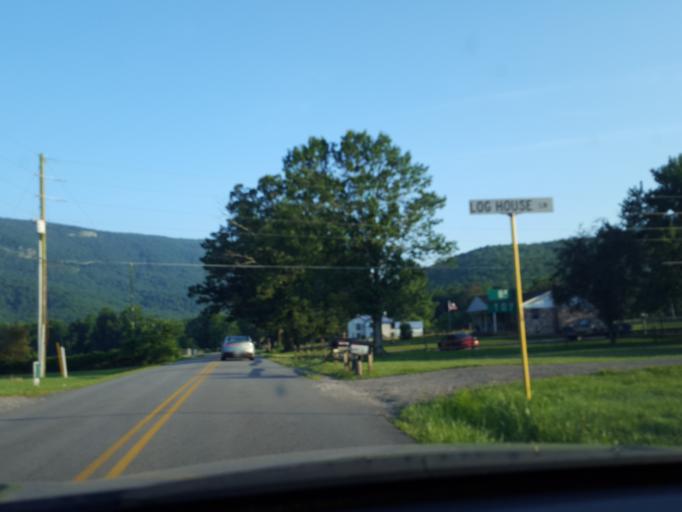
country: US
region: Virginia
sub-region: Augusta County
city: Lyndhurst
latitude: 37.9597
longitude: -78.9620
